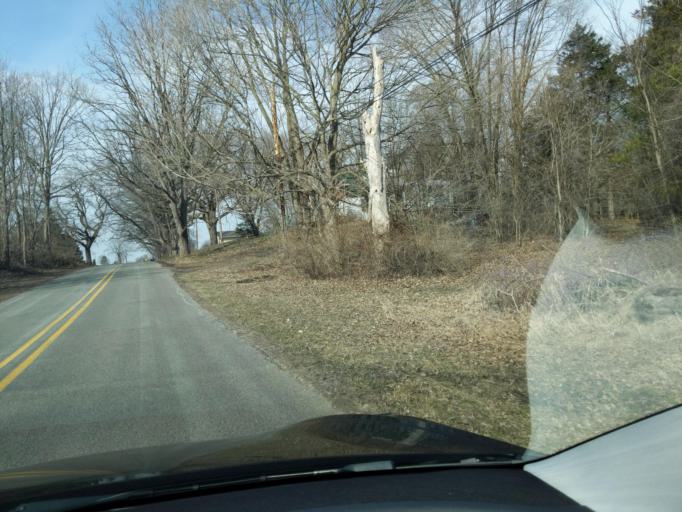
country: US
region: Michigan
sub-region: Ingham County
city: Williamston
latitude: 42.6588
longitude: -84.3047
